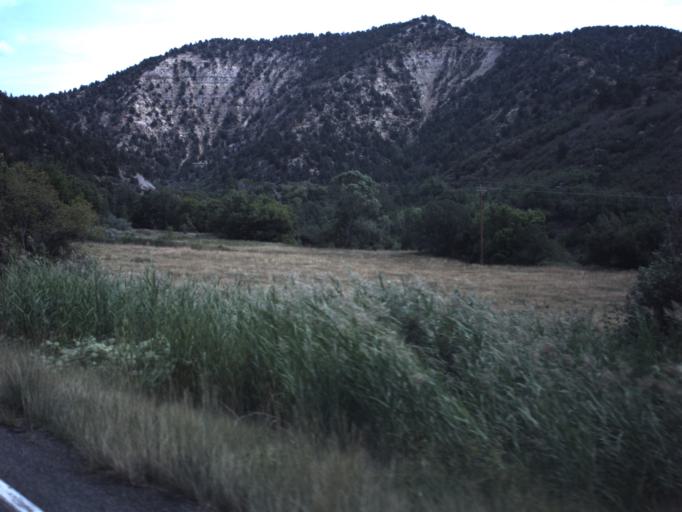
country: US
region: Utah
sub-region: Kane County
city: Kanab
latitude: 37.3600
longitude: -112.5983
